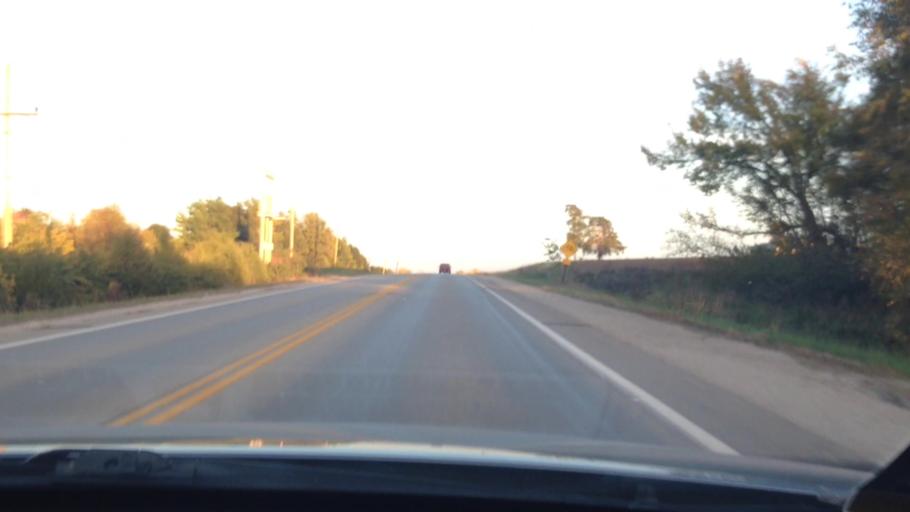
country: US
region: Kansas
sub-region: Johnson County
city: Gardner
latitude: 38.8545
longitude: -94.8903
